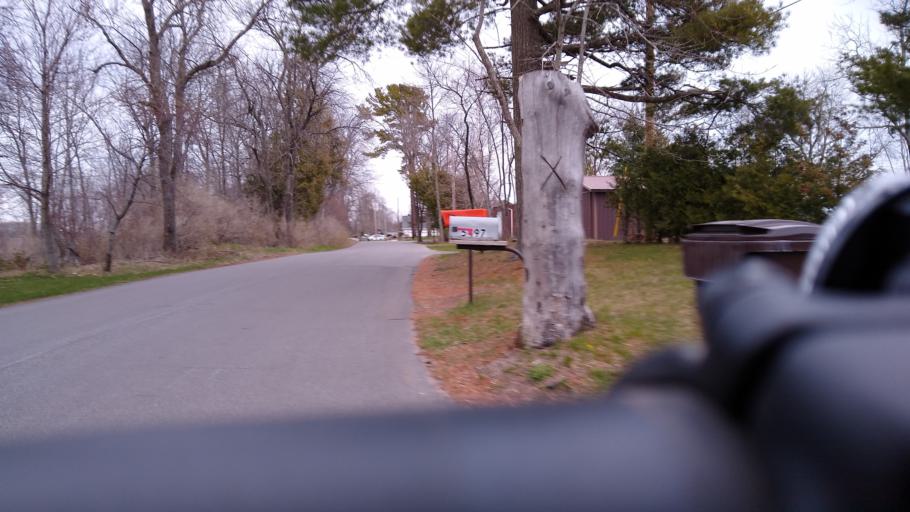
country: US
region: Michigan
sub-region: Delta County
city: Escanaba
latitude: 45.7029
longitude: -87.0913
